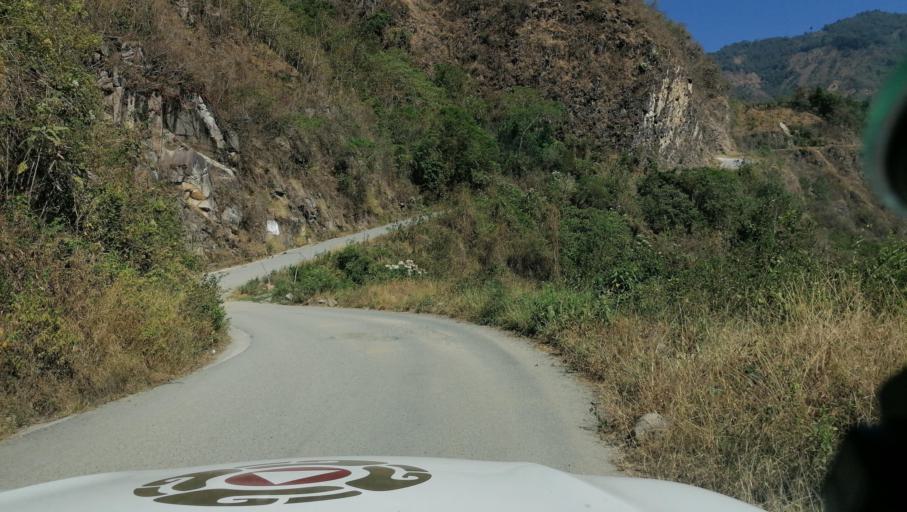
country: GT
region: San Marcos
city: Tacana
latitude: 15.1881
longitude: -92.1860
